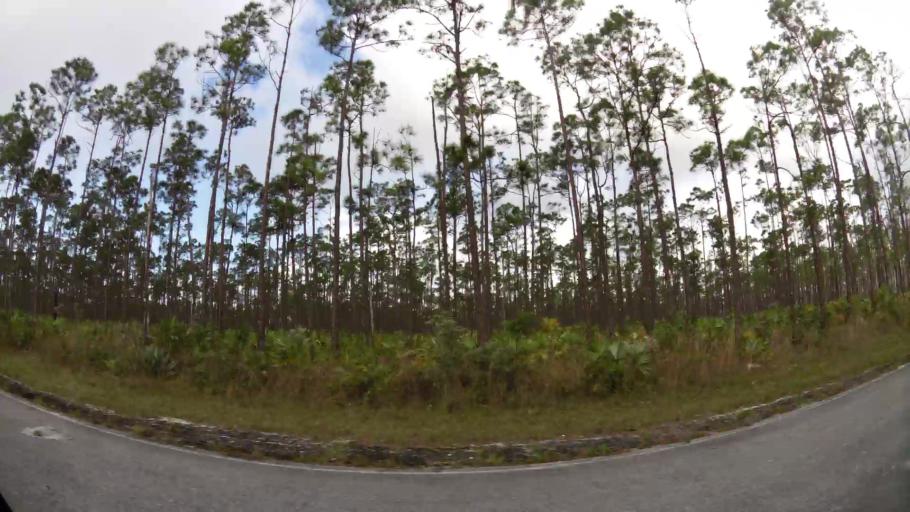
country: BS
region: Freeport
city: Lucaya
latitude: 26.5900
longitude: -78.5461
